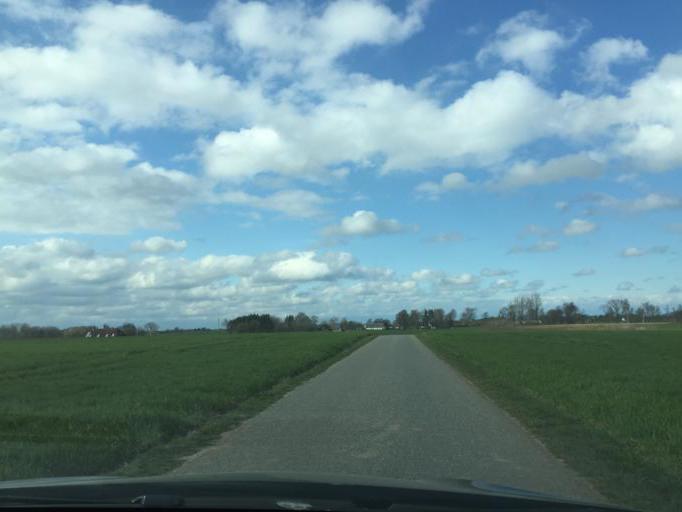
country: DK
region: South Denmark
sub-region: Faaborg-Midtfyn Kommune
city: Arslev
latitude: 55.3244
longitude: 10.4623
